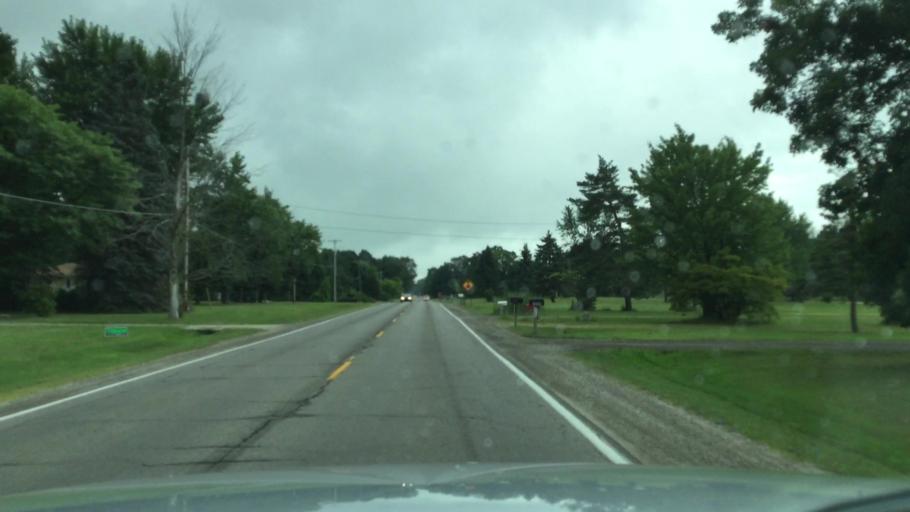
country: US
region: Michigan
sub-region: Genesee County
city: Clio
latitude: 43.1513
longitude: -83.7740
